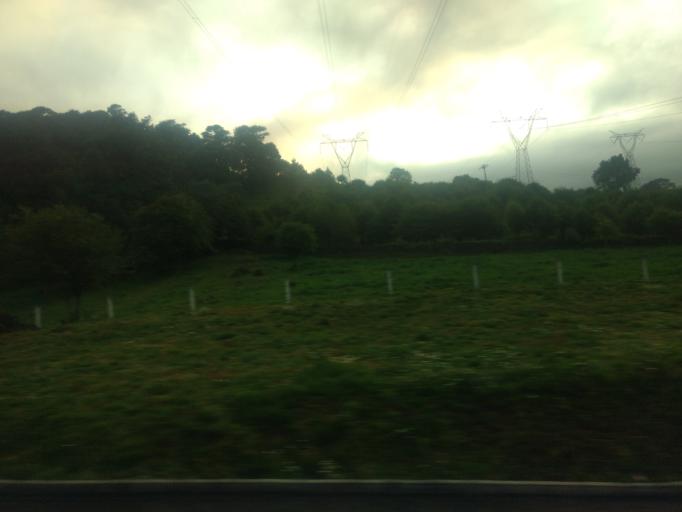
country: MX
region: Veracruz
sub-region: Acajete
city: La Joya
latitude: 19.6302
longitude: -97.0281
